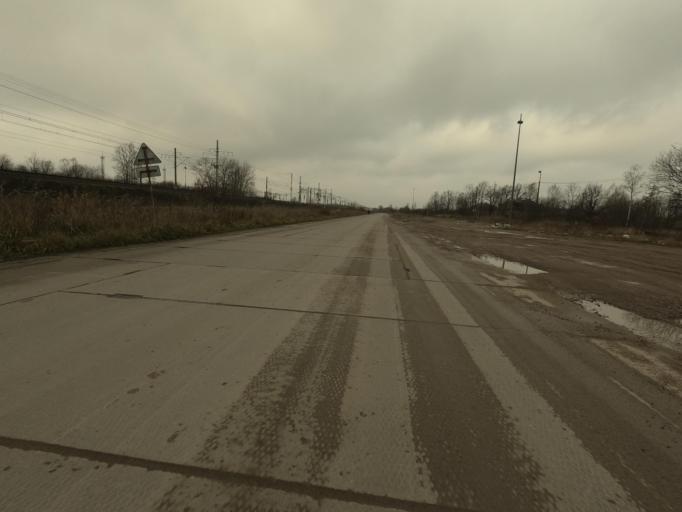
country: RU
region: Leningrad
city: Lyuban'
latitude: 59.4737
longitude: 31.2553
